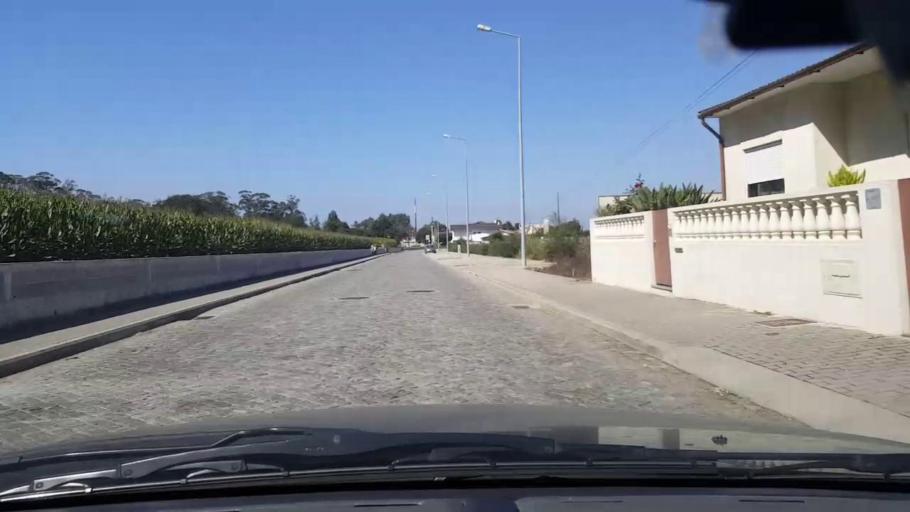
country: PT
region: Porto
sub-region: Vila do Conde
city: Arvore
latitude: 41.3057
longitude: -8.7165
